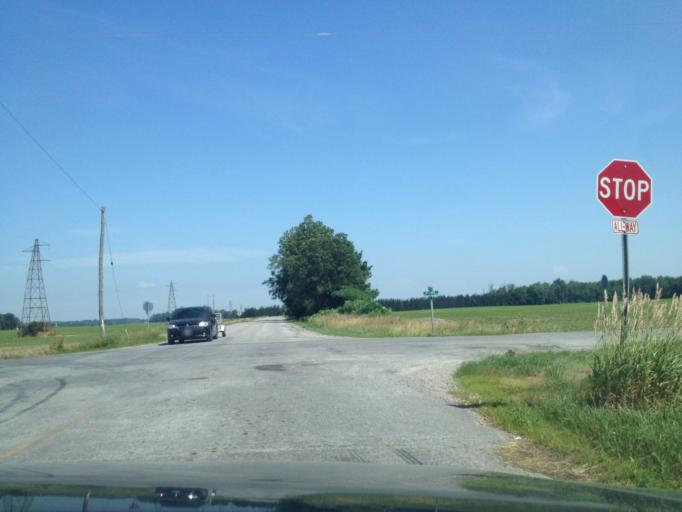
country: CA
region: Ontario
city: London
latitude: 43.0983
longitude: -81.2226
